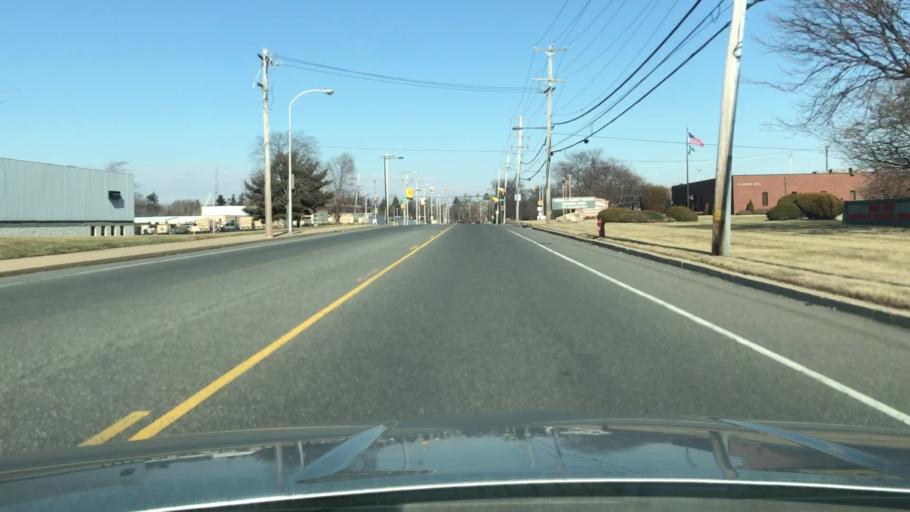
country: US
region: Pennsylvania
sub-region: Bucks County
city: Trevose
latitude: 40.1082
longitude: -74.9868
